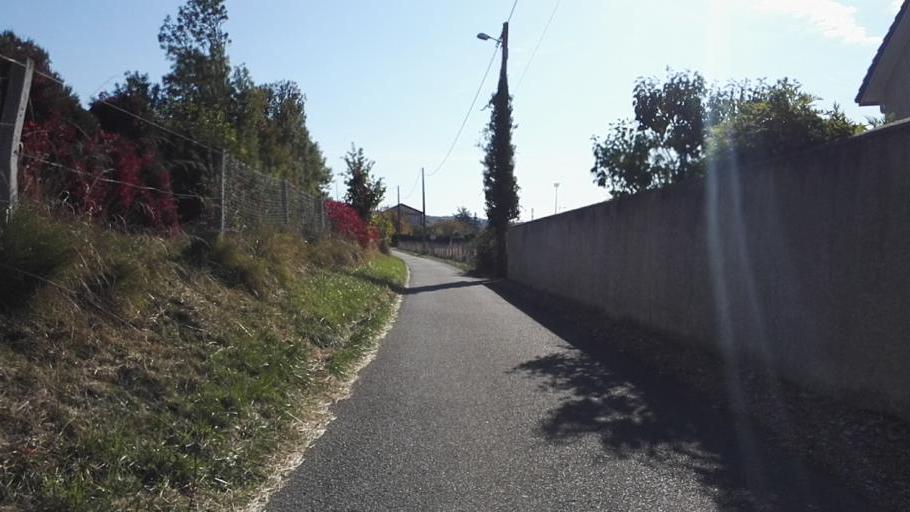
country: FR
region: Haute-Normandie
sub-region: Departement de l'Eure
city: Menilles
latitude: 49.0300
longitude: 1.3692
